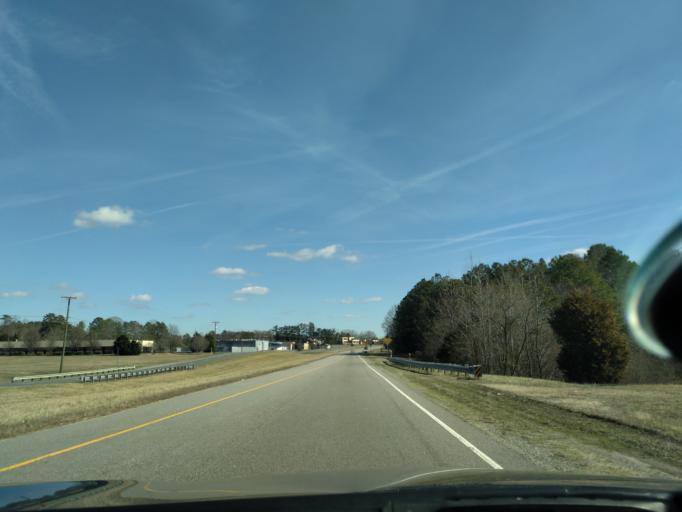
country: US
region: Virginia
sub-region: Nottoway County
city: Crewe
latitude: 37.1903
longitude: -78.1546
